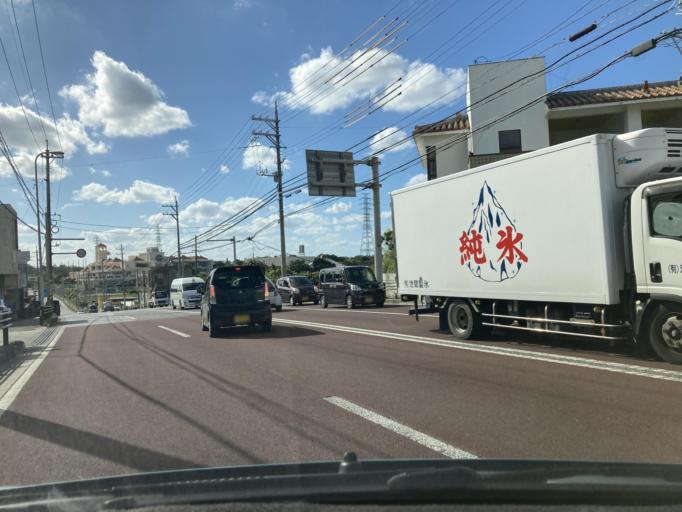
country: JP
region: Okinawa
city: Ishikawa
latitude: 26.3791
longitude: 127.8248
